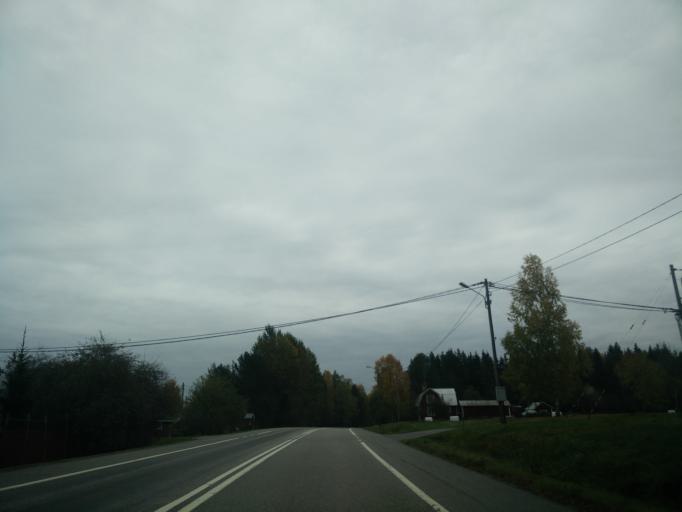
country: SE
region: Gaevleborg
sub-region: Gavle Kommun
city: Norrsundet
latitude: 60.8955
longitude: 17.0914
